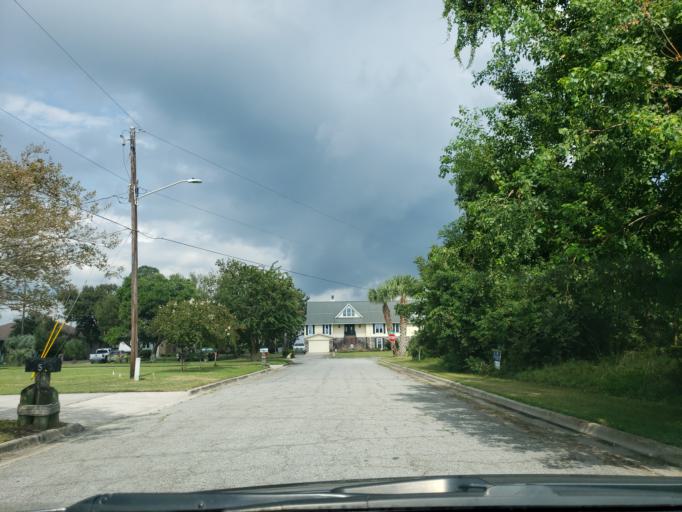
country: US
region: Georgia
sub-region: Chatham County
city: Skidaway Island
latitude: 31.9287
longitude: -81.0823
